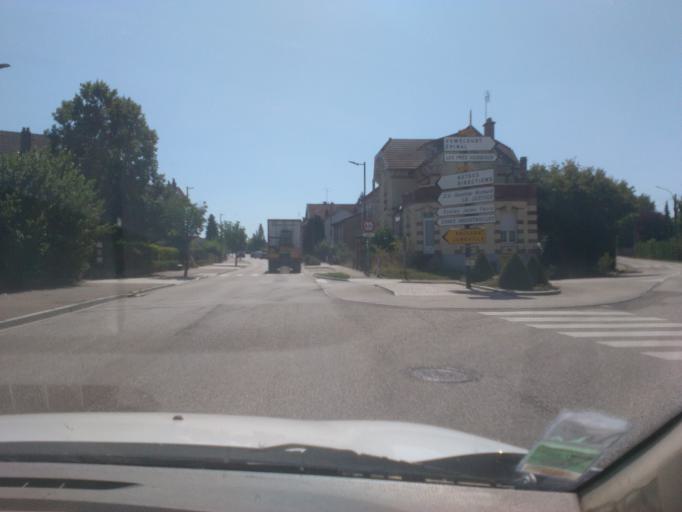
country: FR
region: Lorraine
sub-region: Departement des Vosges
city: Rambervillers
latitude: 48.3376
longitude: 6.6352
